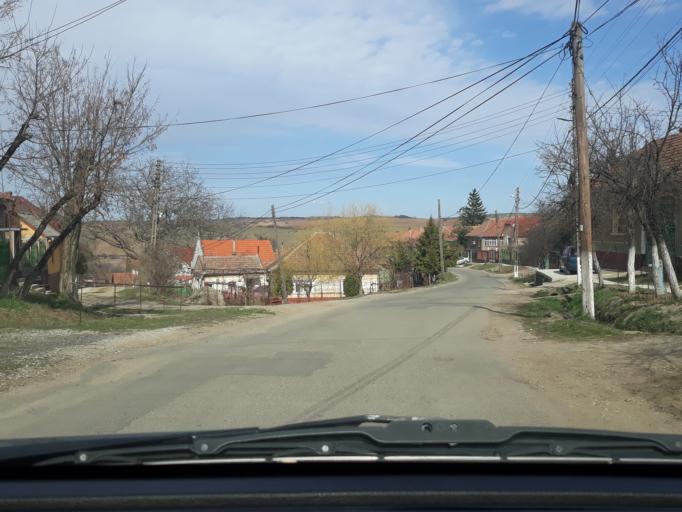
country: RO
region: Bihor
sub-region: Comuna Paleu
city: Paleu
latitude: 47.1158
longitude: 21.9577
